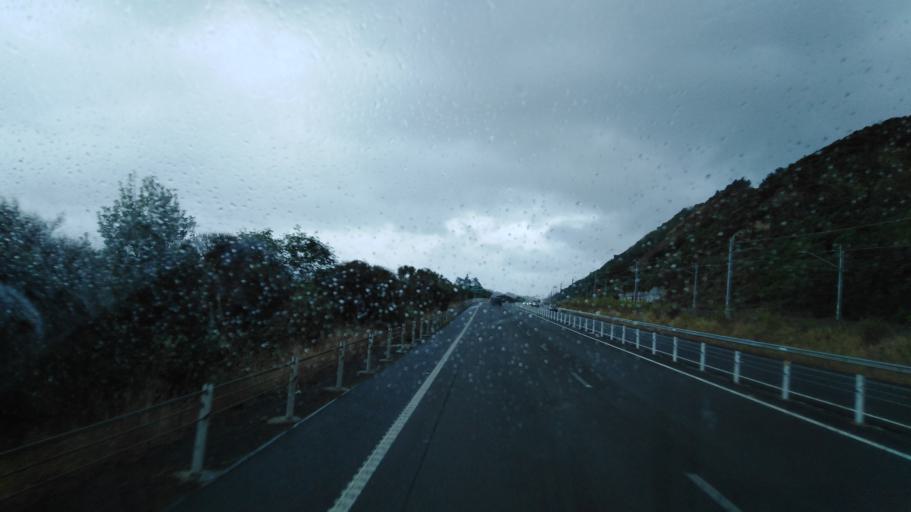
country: NZ
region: Wellington
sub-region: Kapiti Coast District
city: Paraparaumu
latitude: -40.9545
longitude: 174.9884
